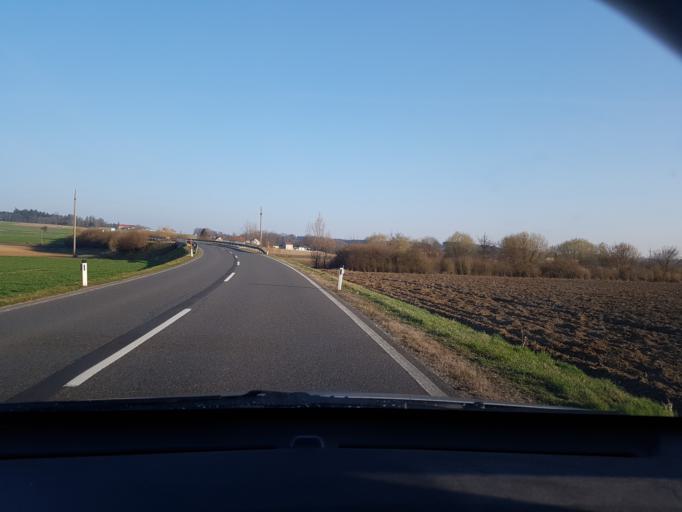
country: AT
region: Upper Austria
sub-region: Politischer Bezirk Linz-Land
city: Ansfelden
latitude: 48.1749
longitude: 14.2510
